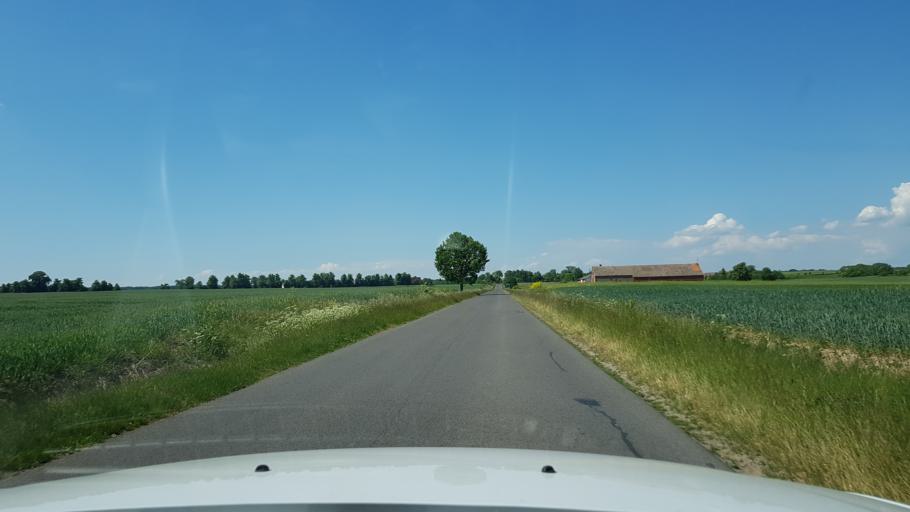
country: PL
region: West Pomeranian Voivodeship
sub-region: Powiat gryfinski
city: Banie
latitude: 53.0728
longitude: 14.6193
